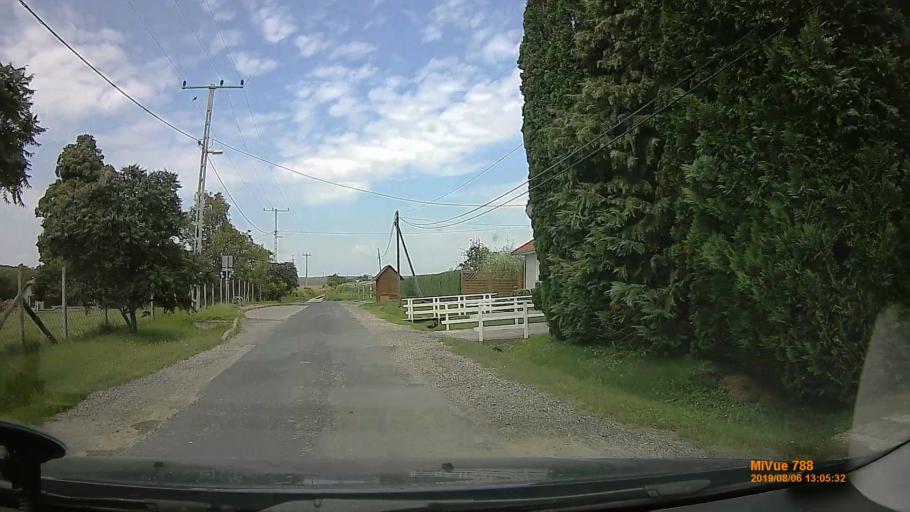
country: HU
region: Zala
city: Pacsa
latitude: 46.6301
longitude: 17.0453
